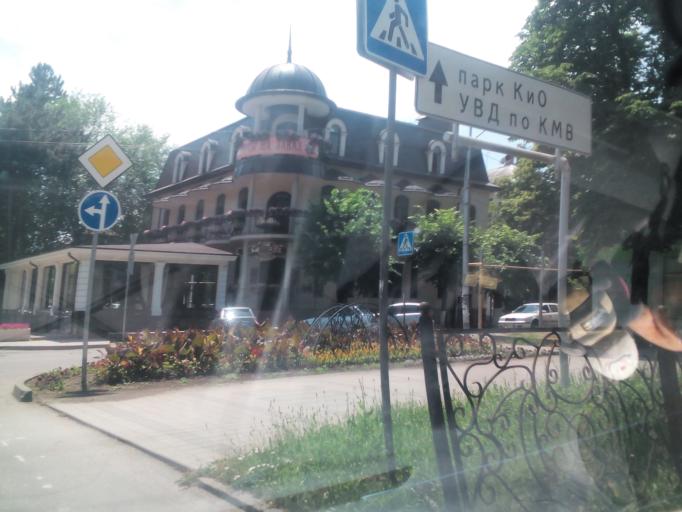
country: RU
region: Stavropol'skiy
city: Pyatigorsk
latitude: 44.0359
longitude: 43.0621
